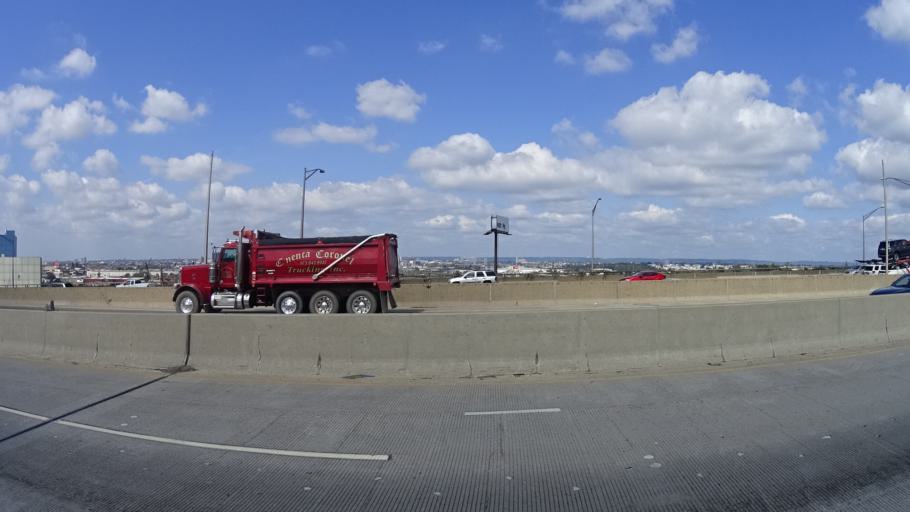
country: US
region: New Jersey
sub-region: Hudson County
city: Harrison
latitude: 40.7402
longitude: -74.1230
